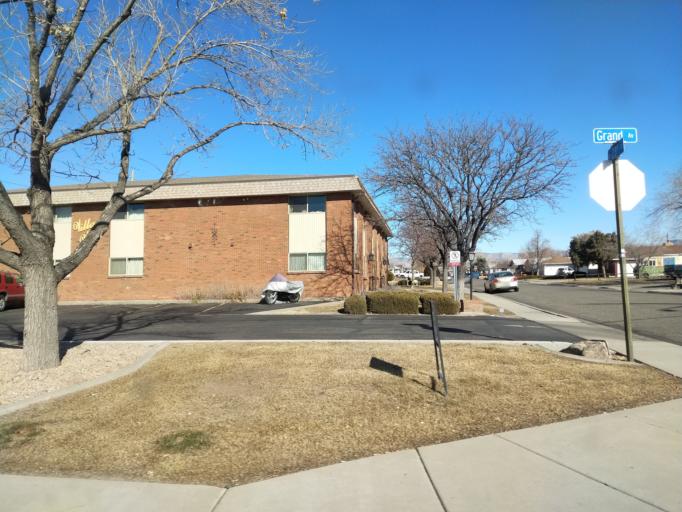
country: US
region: Colorado
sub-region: Mesa County
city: Grand Junction
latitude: 39.0702
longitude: -108.5385
